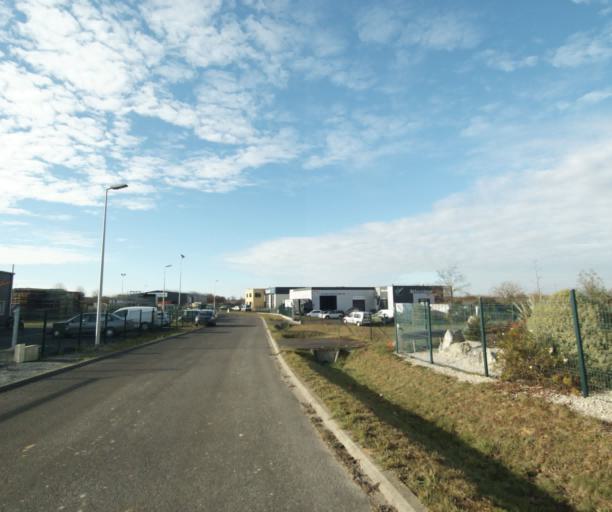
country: FR
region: Poitou-Charentes
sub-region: Departement de la Charente-Maritime
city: Corme-Royal
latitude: 45.7027
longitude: -0.7898
